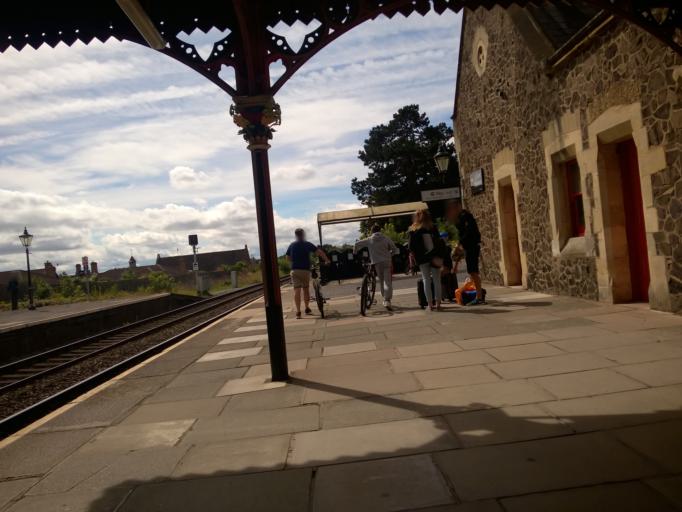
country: GB
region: England
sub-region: Worcestershire
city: Great Malvern
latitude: 52.1091
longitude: -2.3184
